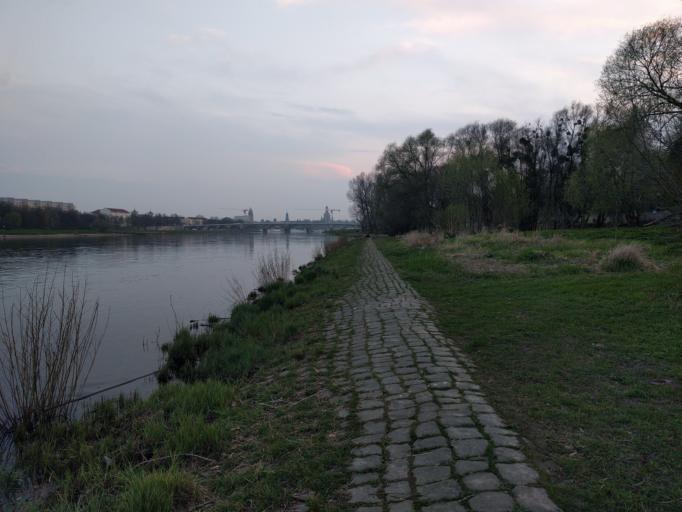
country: DE
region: Saxony
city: Albertstadt
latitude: 51.0622
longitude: 13.7638
